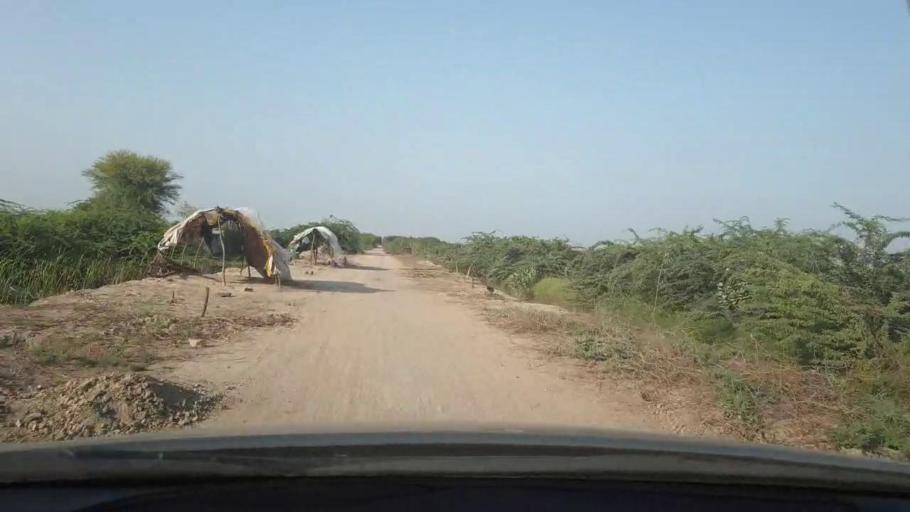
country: PK
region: Sindh
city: Naukot
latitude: 24.7771
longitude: 69.2329
